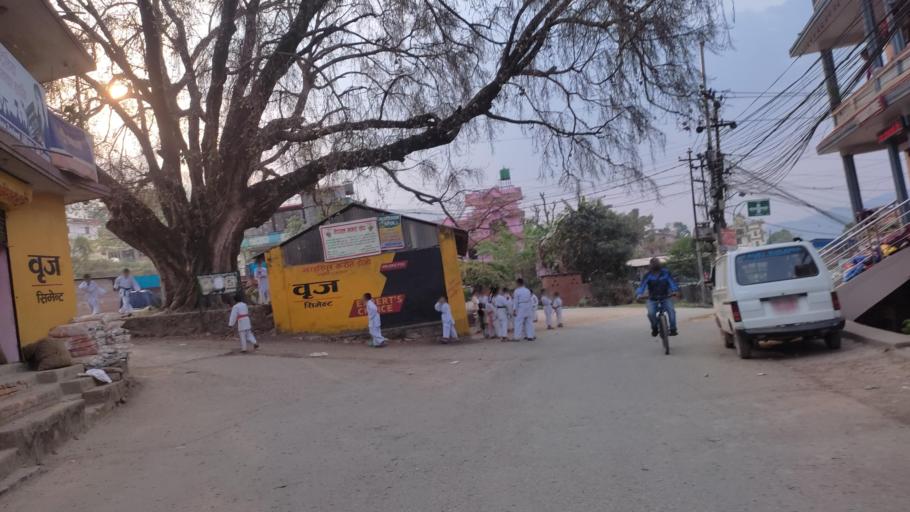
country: NP
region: Central Region
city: Kirtipur
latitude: 27.6706
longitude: 85.2487
